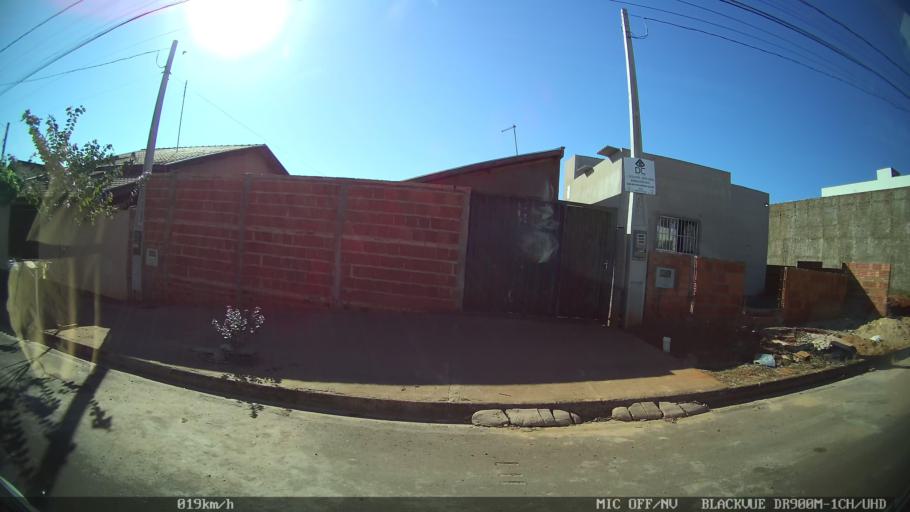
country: BR
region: Sao Paulo
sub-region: Olimpia
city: Olimpia
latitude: -20.7405
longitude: -48.8825
